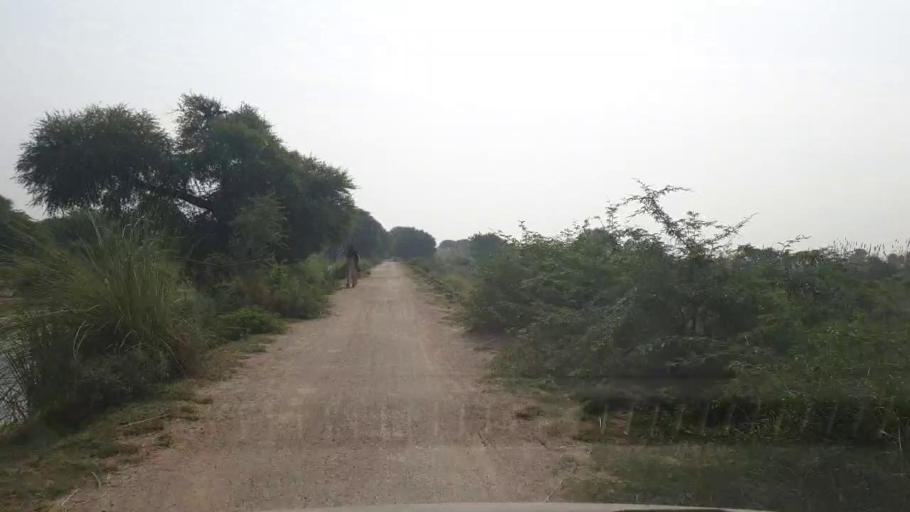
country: PK
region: Sindh
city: Tando Muhammad Khan
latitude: 25.1247
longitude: 68.4368
